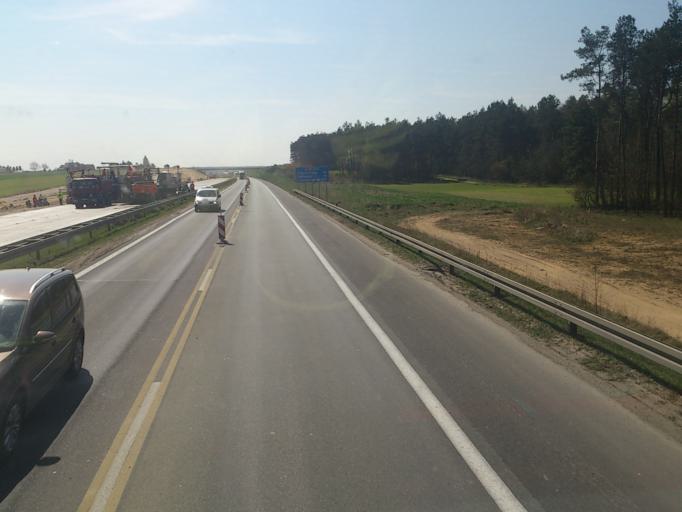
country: PL
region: Lodz Voivodeship
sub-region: Powiat piotrkowski
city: Grabica
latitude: 51.5400
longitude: 19.6017
